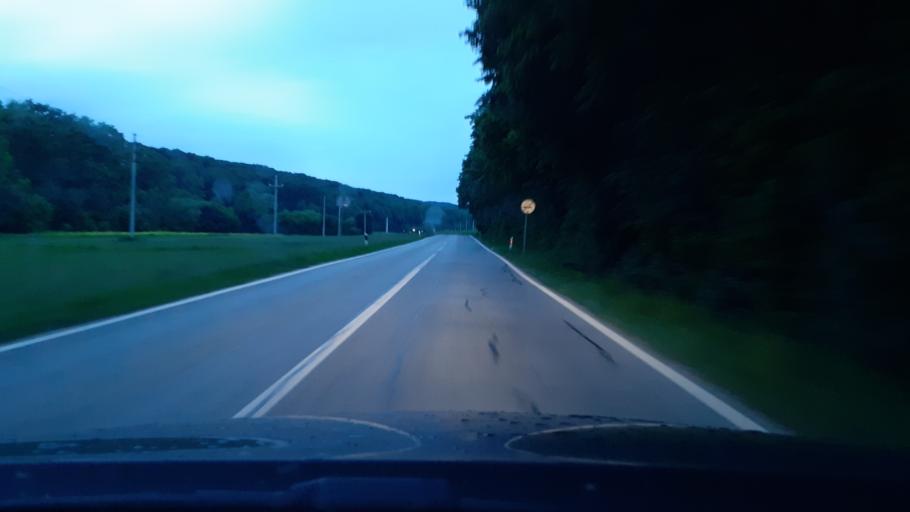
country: HR
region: Pozesko-Slavonska
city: Bilice
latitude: 45.1896
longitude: 17.8549
